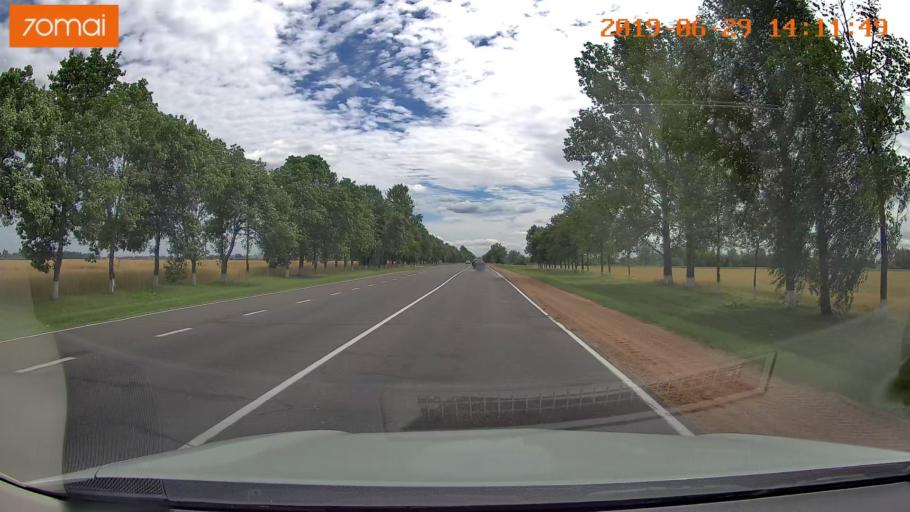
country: BY
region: Minsk
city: Salihorsk
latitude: 52.8159
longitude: 27.5048
